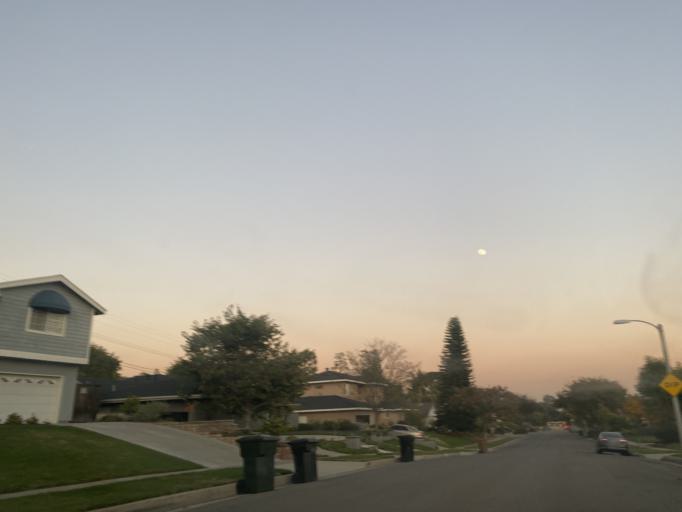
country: US
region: California
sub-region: Orange County
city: Fullerton
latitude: 33.8846
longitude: -117.9019
